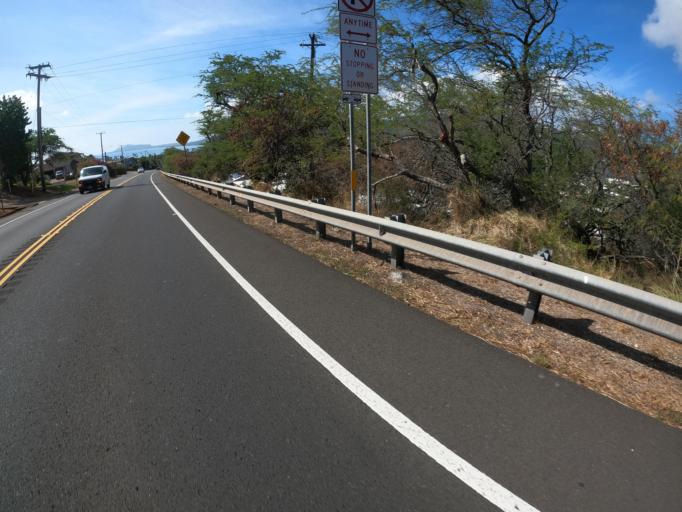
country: US
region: Hawaii
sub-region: Honolulu County
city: Waimanalo Beach
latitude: 21.2751
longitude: -157.6978
